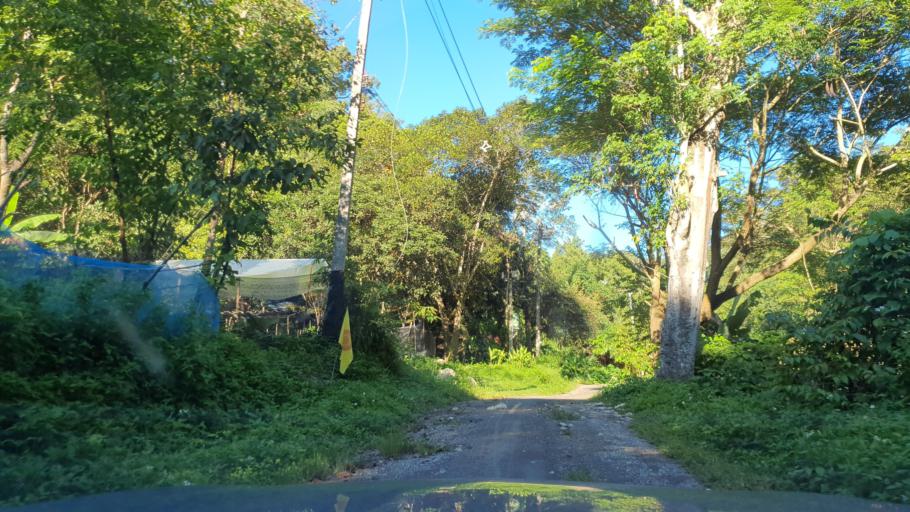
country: TH
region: Chiang Mai
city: Mae On
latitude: 18.8159
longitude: 99.3379
